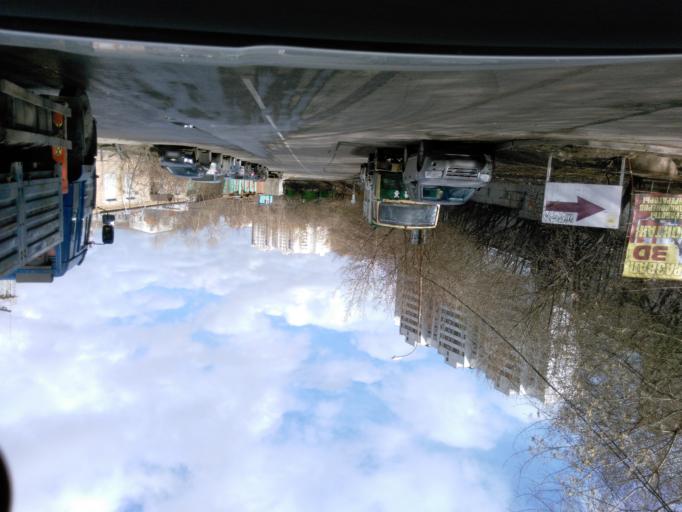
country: RU
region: Moscow
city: Novyye Cheremushki
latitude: 55.6947
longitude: 37.5960
